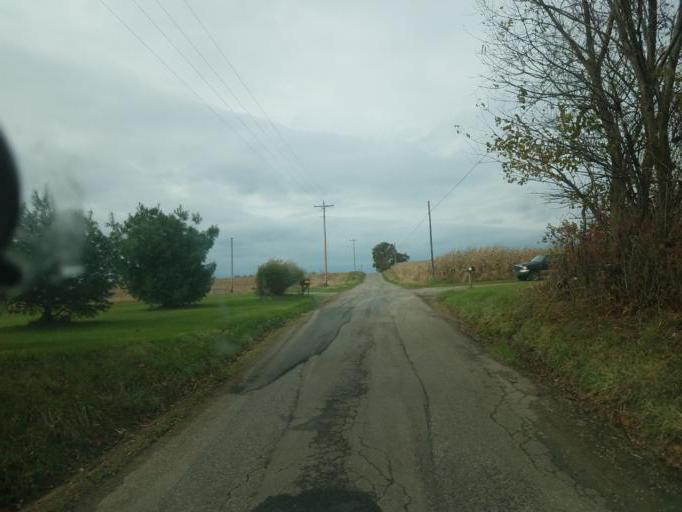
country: US
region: Ohio
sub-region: Wayne County
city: Shreve
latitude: 40.6281
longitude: -82.1170
